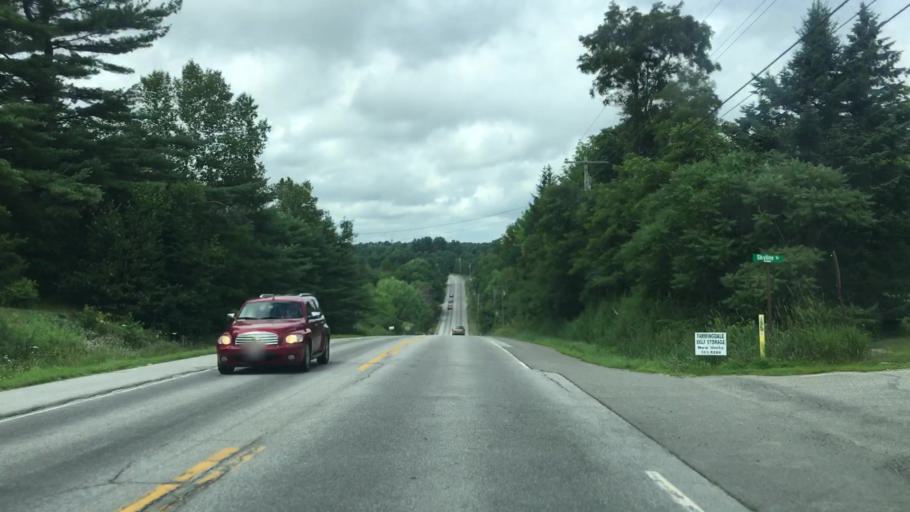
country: US
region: Maine
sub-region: Kennebec County
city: Farmingdale
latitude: 44.2669
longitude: -69.7651
